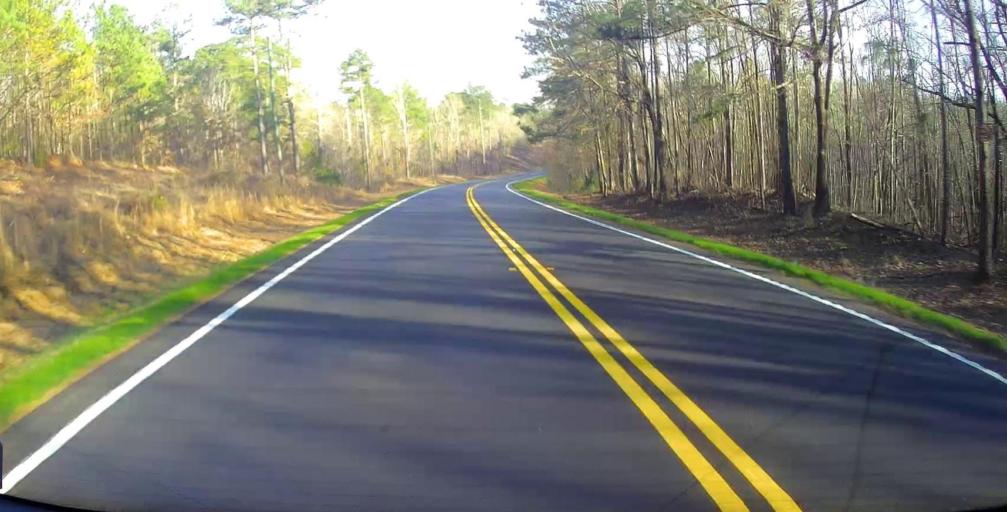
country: US
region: Georgia
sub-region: Harris County
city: Hamilton
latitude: 32.7461
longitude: -84.9804
